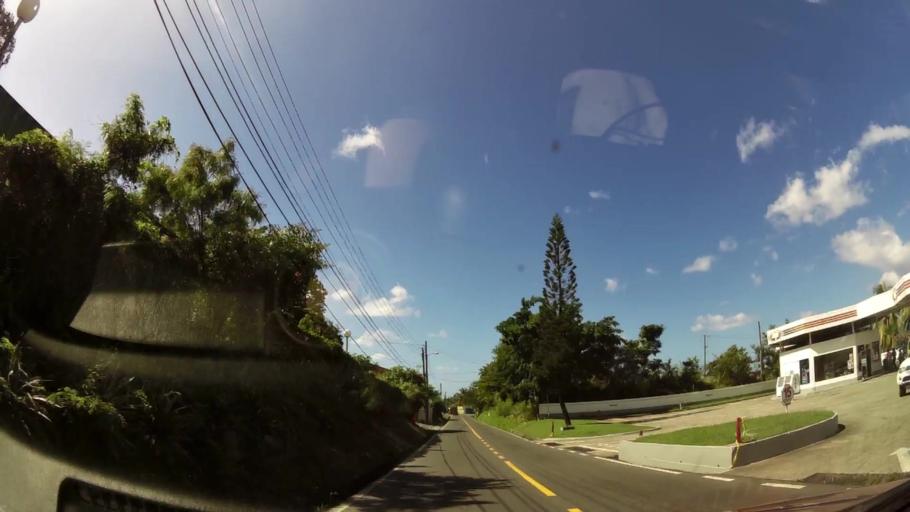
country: DM
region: Saint George
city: Roseau
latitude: 15.3286
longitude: -61.3933
